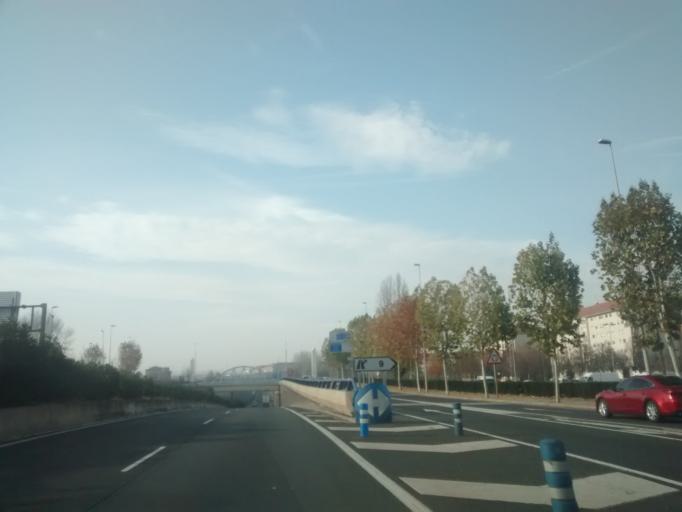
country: ES
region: La Rioja
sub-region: Provincia de La Rioja
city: Logrono
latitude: 42.4547
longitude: -2.4544
